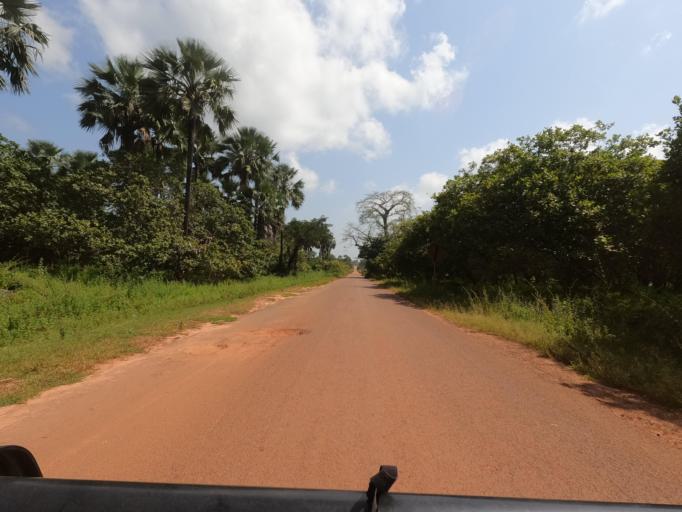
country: GW
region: Cacheu
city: Canchungo
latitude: 12.2849
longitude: -15.7818
